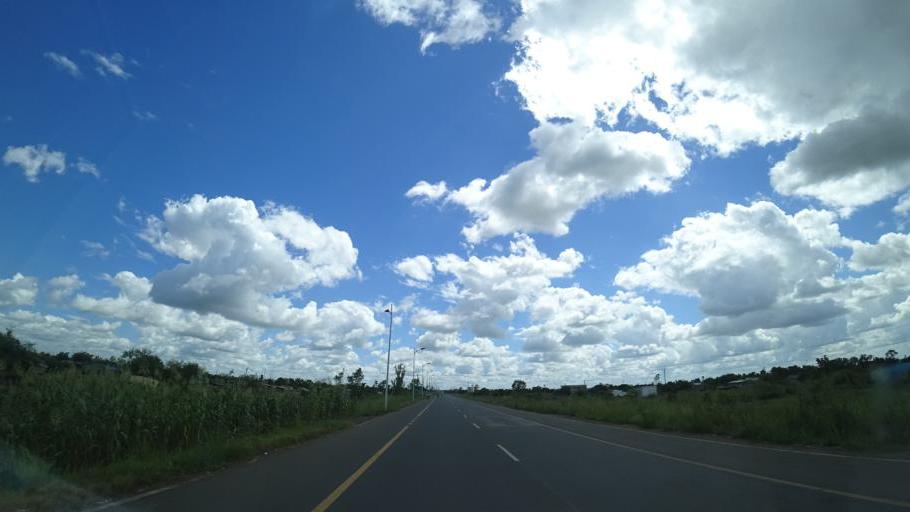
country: MZ
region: Sofala
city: Dondo
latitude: -19.2796
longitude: 34.2193
